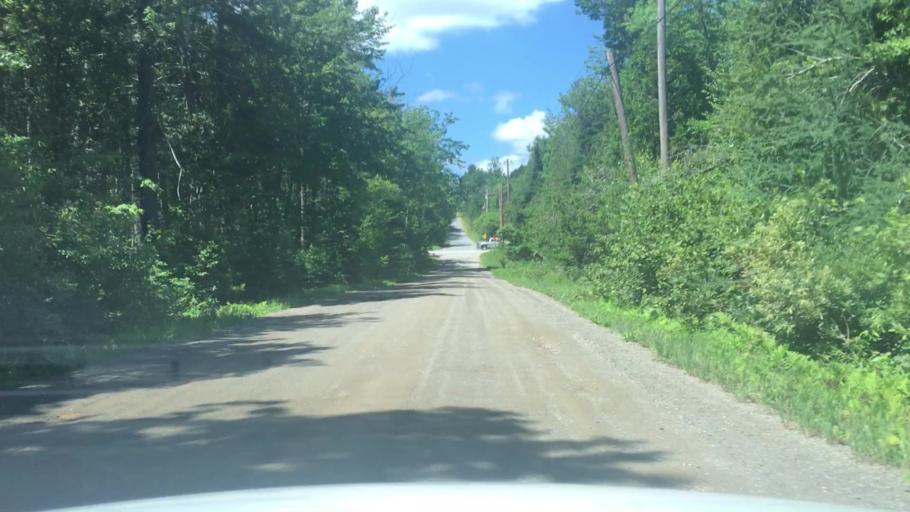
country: US
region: Maine
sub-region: Waldo County
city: Northport
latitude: 44.3462
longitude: -68.9679
